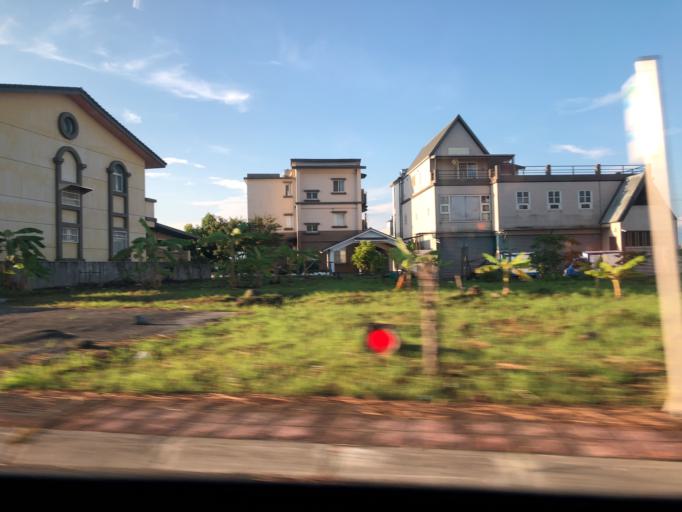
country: TW
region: Taiwan
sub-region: Yilan
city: Yilan
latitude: 24.7492
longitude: 121.7775
